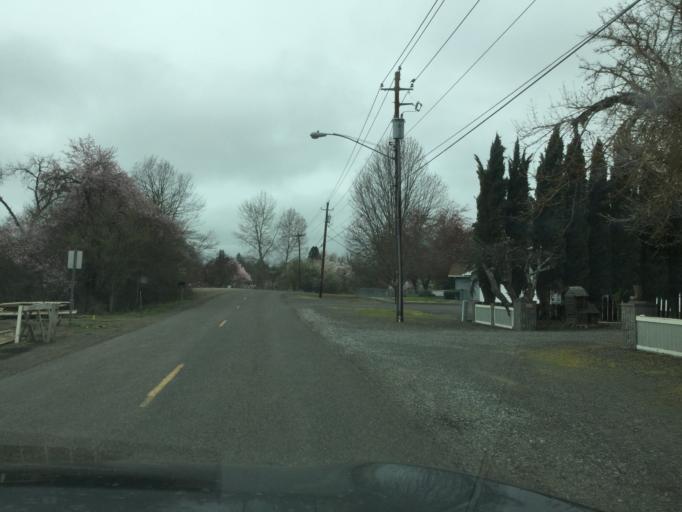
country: US
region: Oregon
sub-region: Jackson County
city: Central Point
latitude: 42.3926
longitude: -122.9189
